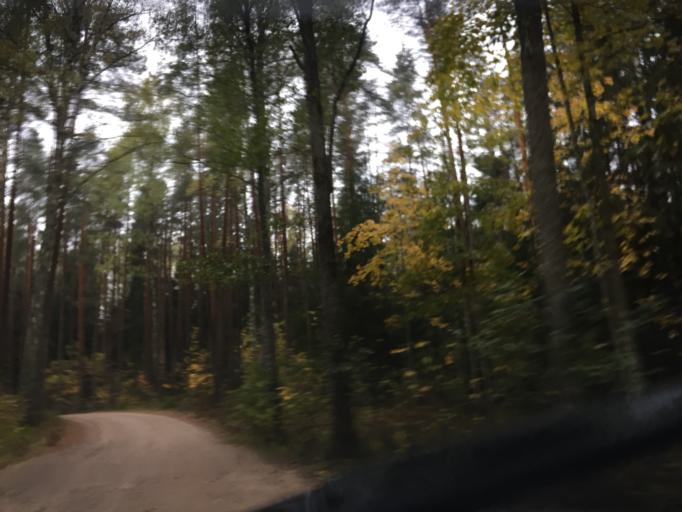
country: LV
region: Engure
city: Smarde
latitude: 56.9196
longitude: 23.4700
